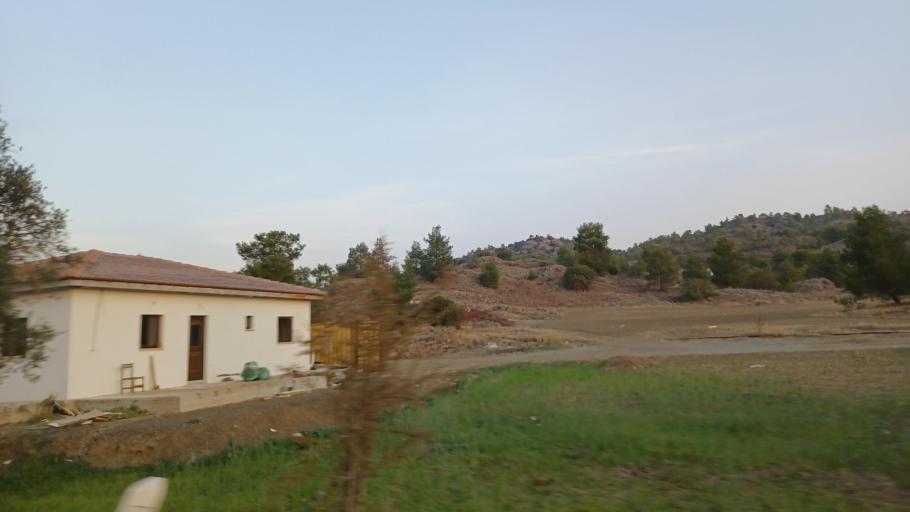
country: CY
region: Larnaka
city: Kornos
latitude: 34.9139
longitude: 33.3683
